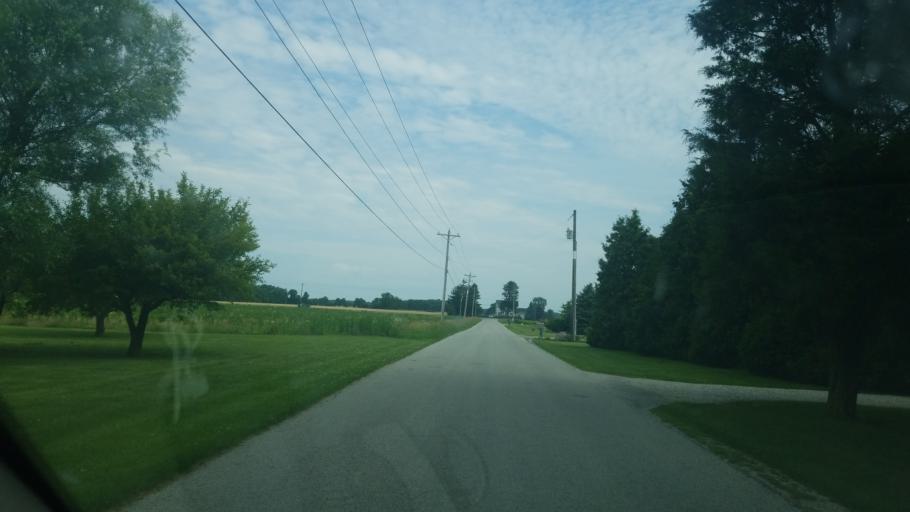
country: US
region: Ohio
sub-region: Seneca County
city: Fostoria
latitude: 41.0701
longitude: -83.4634
